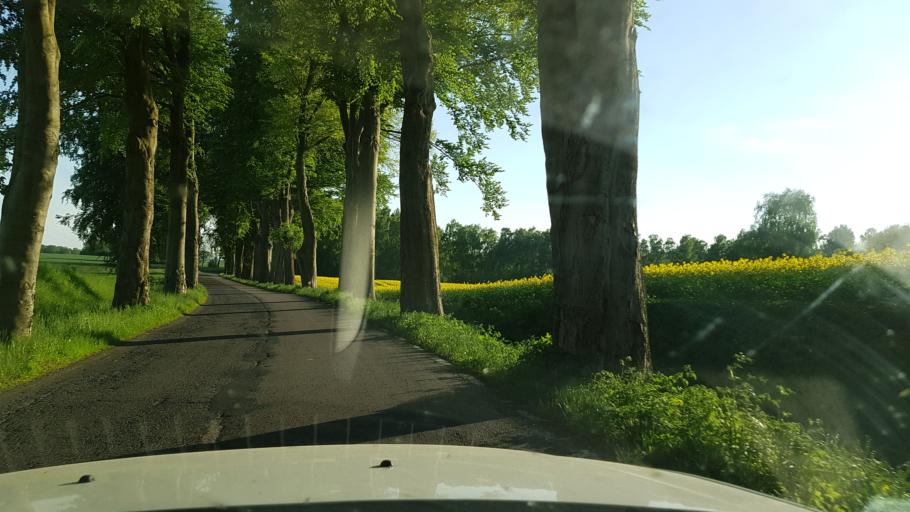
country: PL
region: West Pomeranian Voivodeship
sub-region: Powiat lobeski
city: Dobra
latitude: 53.5818
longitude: 15.2783
